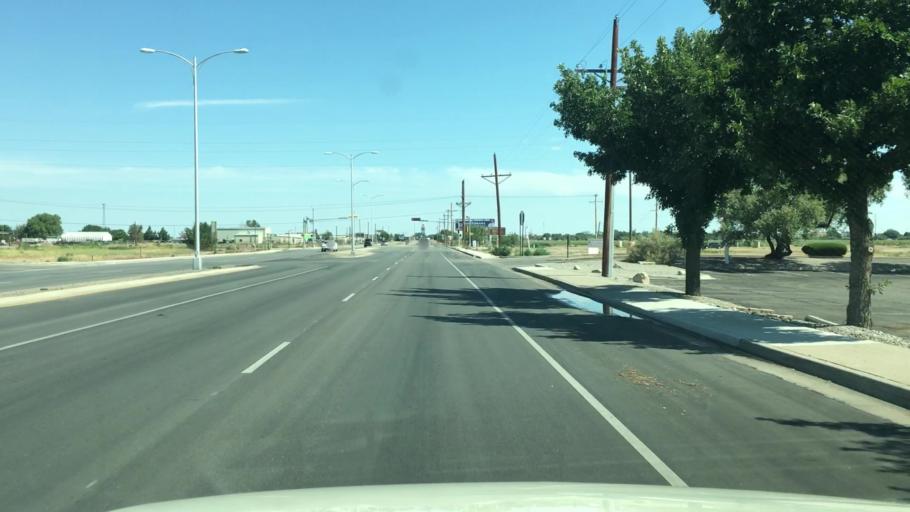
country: US
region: New Mexico
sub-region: Chaves County
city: Roswell
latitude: 33.4506
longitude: -104.5233
